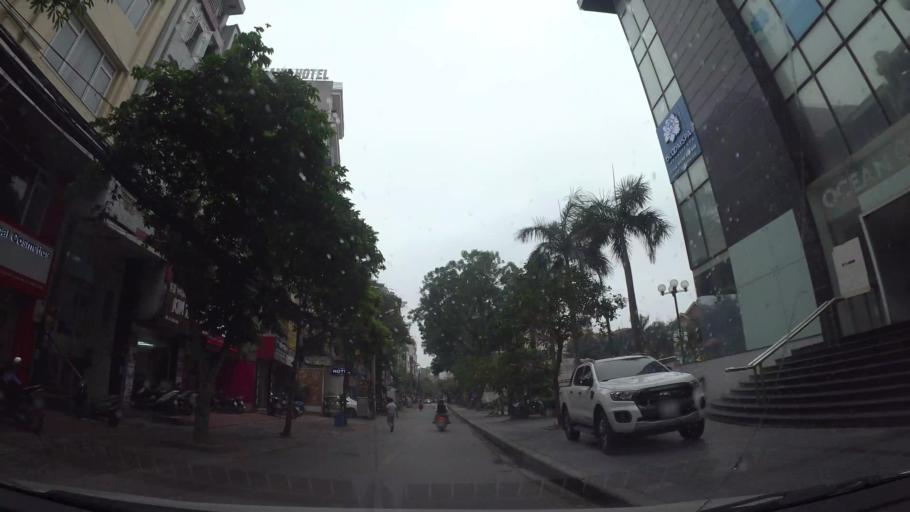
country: VN
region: Ha Noi
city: Thanh Xuan
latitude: 21.0134
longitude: 105.8019
